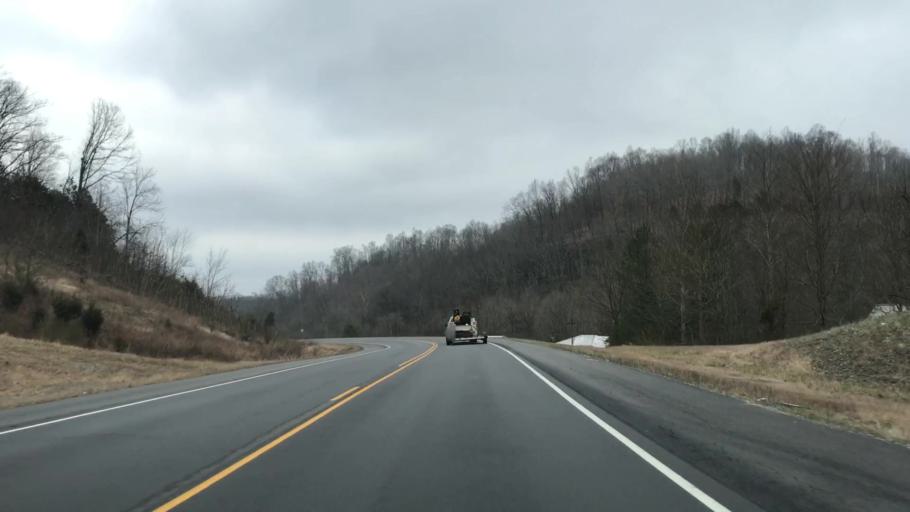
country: US
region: Kentucky
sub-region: Cumberland County
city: Burkesville
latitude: 36.8965
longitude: -85.4282
